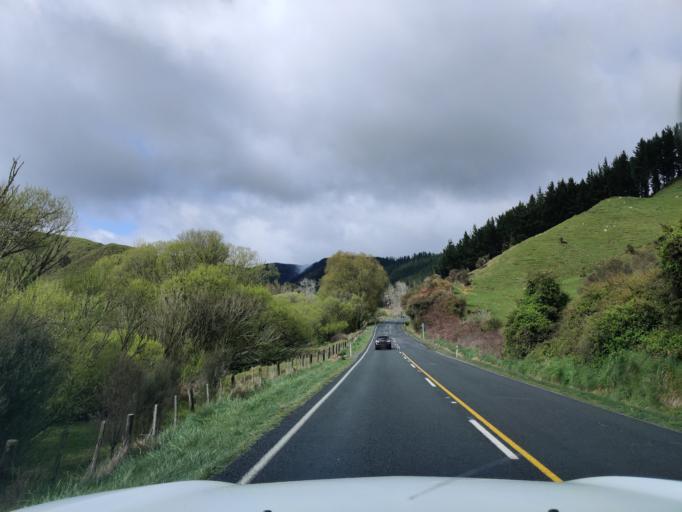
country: NZ
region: Waikato
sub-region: Otorohanga District
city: Otorohanga
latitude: -38.6113
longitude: 175.2180
